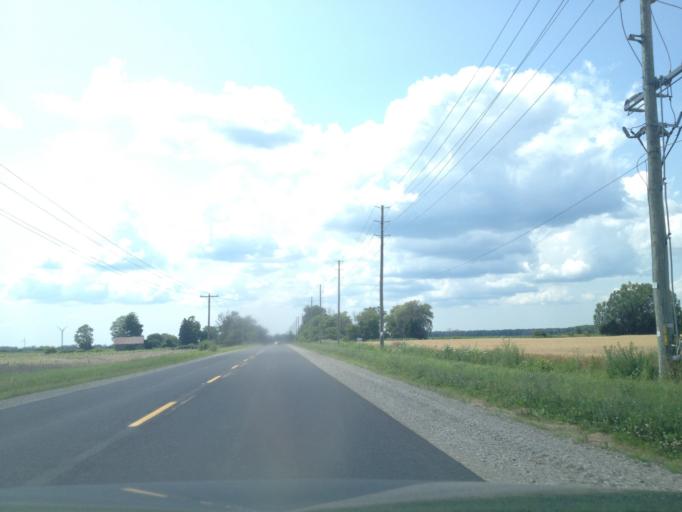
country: CA
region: Ontario
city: Aylmer
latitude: 42.6688
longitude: -80.8397
